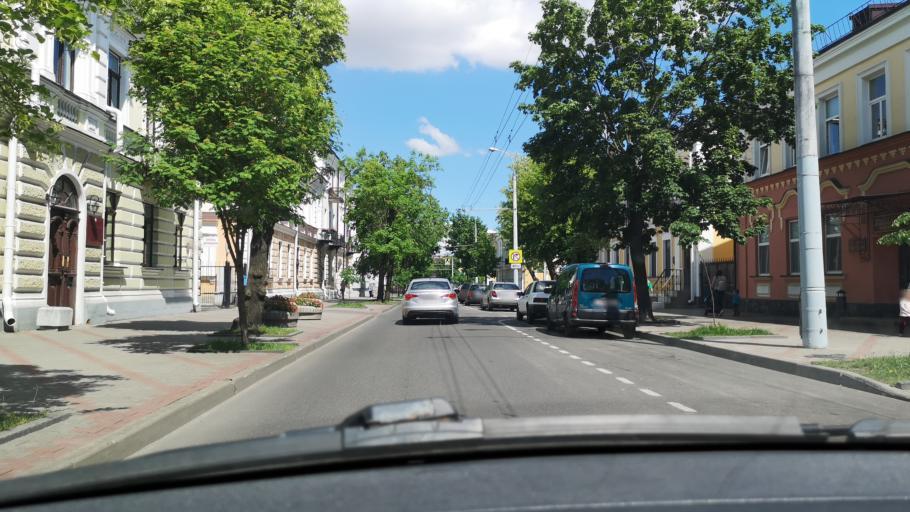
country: BY
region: Brest
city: Brest
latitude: 52.0892
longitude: 23.6889
